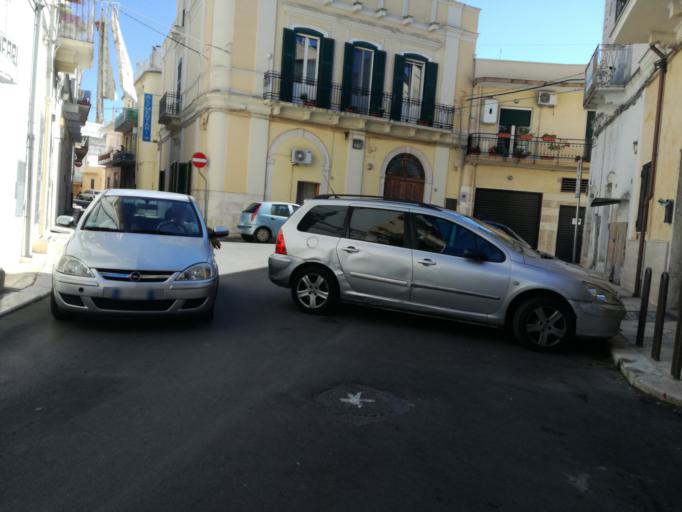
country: IT
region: Apulia
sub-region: Provincia di Bari
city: Triggiano
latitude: 41.0632
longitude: 16.9204
